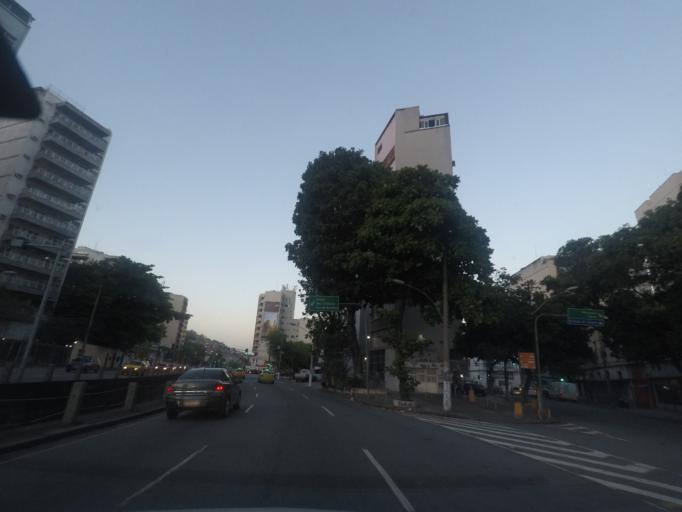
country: BR
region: Rio de Janeiro
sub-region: Rio De Janeiro
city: Rio de Janeiro
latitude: -22.9149
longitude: -43.2341
